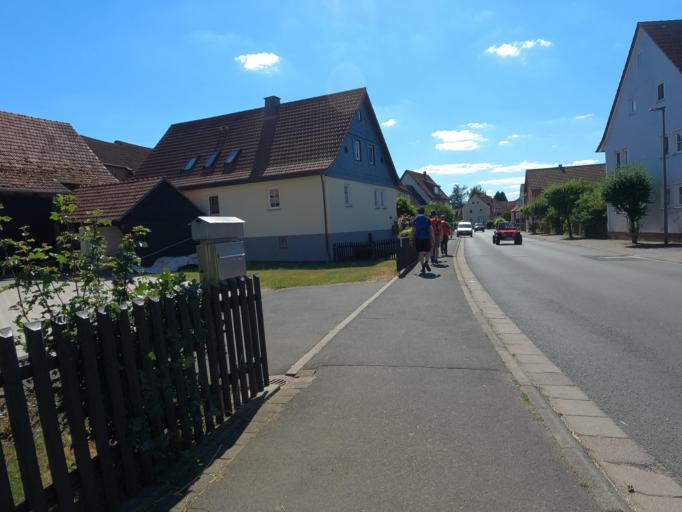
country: DE
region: Hesse
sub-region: Regierungsbezirk Darmstadt
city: Schluchtern
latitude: 50.3595
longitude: 9.5541
